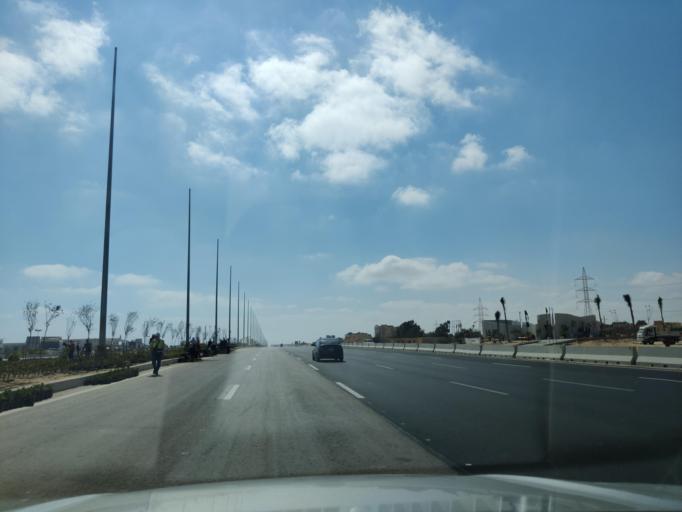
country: EG
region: Muhafazat Matruh
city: Al `Alamayn
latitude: 30.9923
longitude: 28.6728
